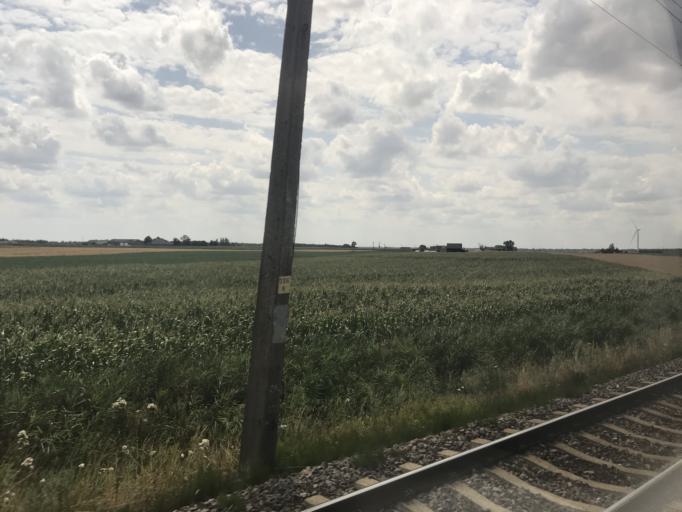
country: PL
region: Greater Poland Voivodeship
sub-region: Powiat poznanski
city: Buk
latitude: 52.3370
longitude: 16.4991
